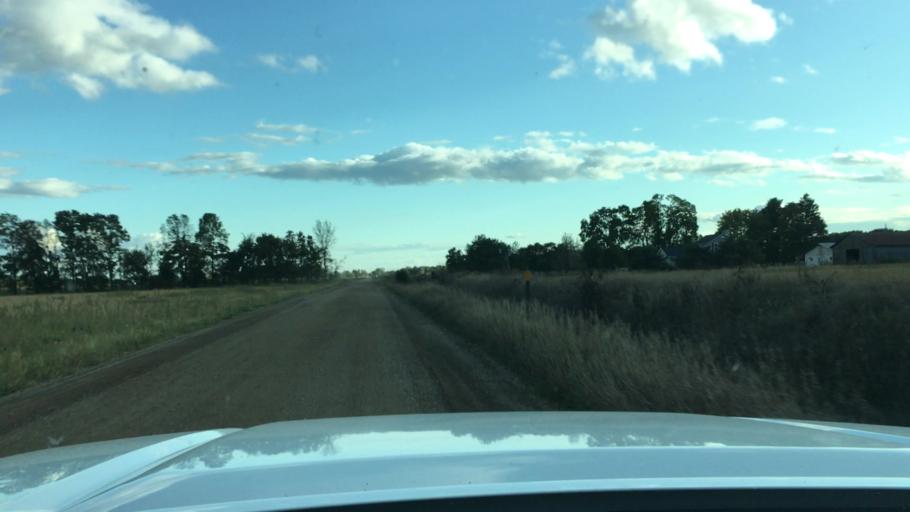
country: US
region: Michigan
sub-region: Clinton County
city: Saint Johns
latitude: 43.0836
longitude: -84.4839
